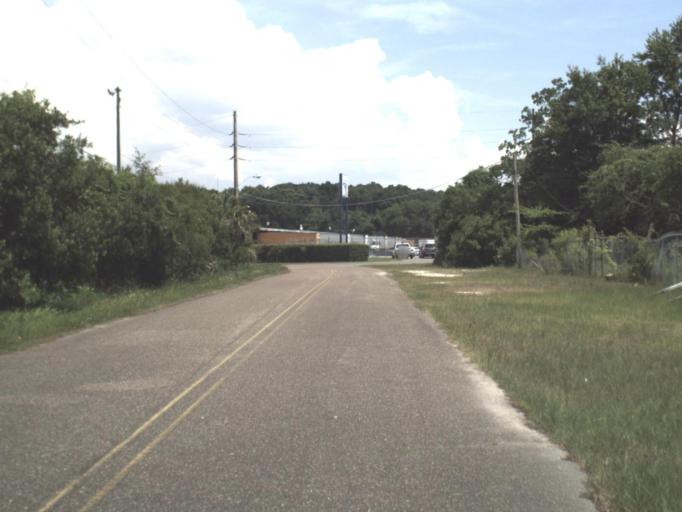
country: US
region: Florida
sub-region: Duval County
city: Jacksonville
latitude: 30.3666
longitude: -81.7240
